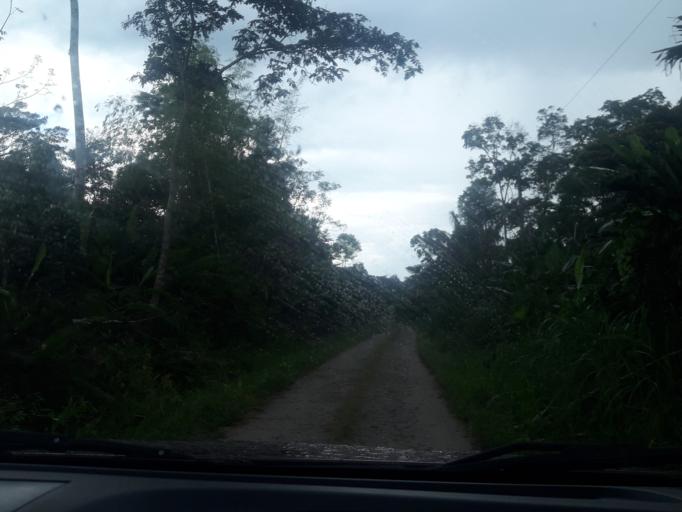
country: EC
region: Napo
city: Tena
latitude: -1.0975
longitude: -77.6816
